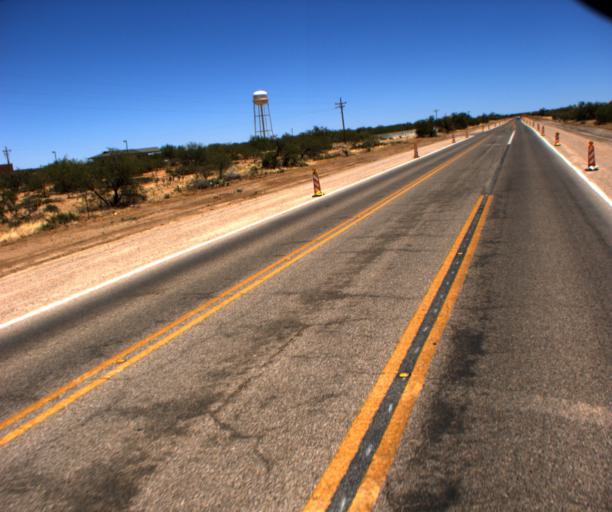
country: US
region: Arizona
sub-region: Pima County
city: Sells
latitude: 31.9875
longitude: -111.7159
